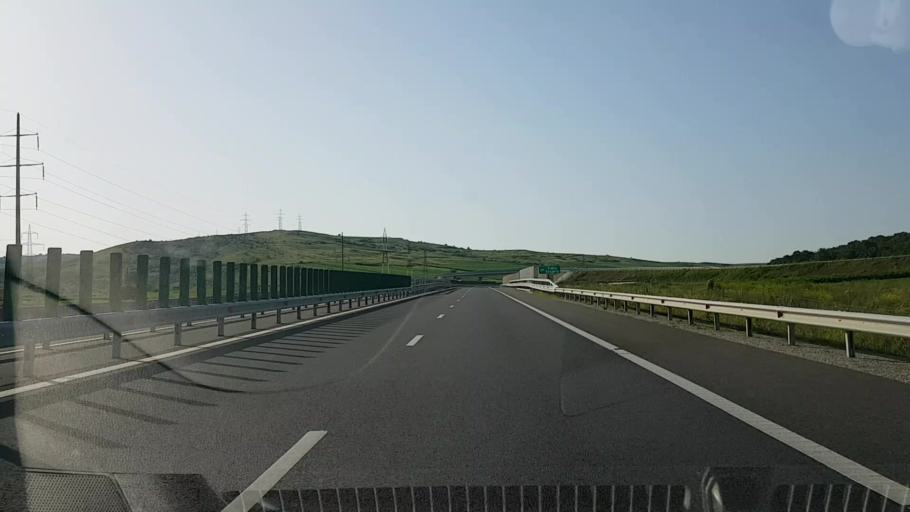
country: RO
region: Alba
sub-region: Comuna Unirea
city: Unirea
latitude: 46.4649
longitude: 23.7792
